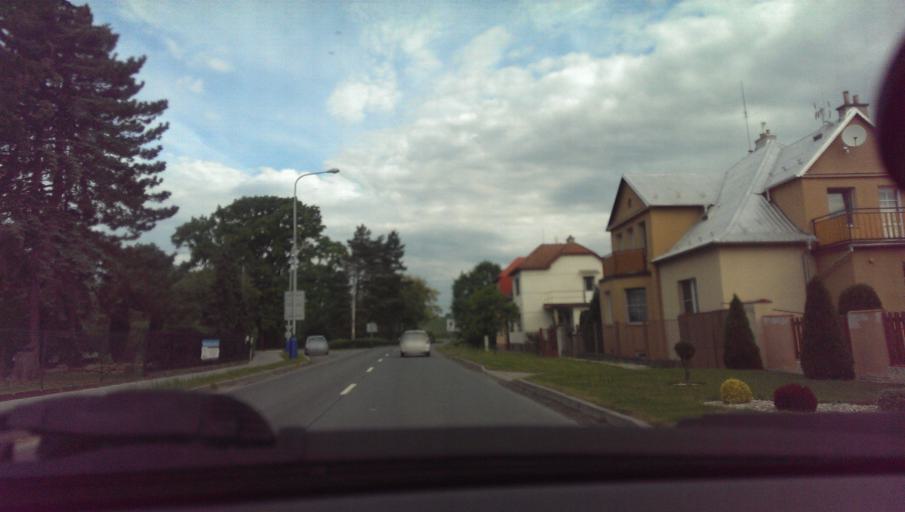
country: CZ
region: Zlin
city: Kvasice
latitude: 49.2436
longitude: 17.4679
